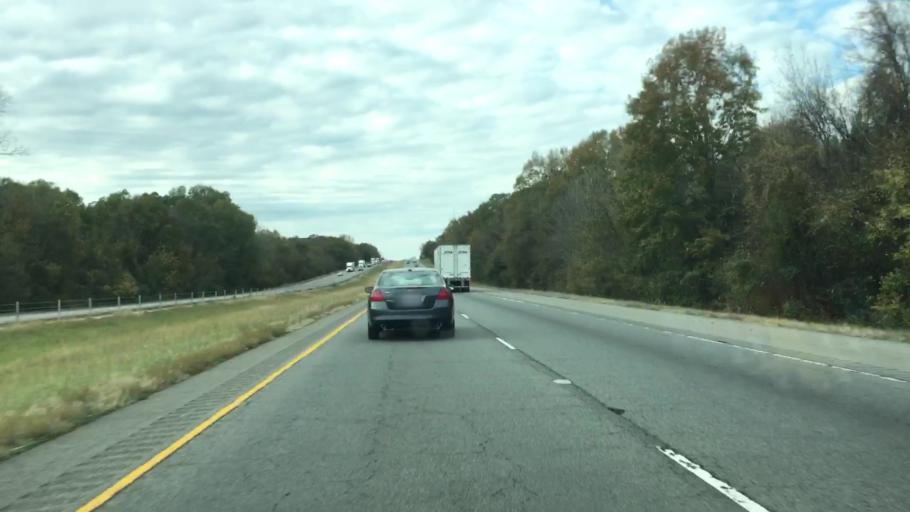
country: US
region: Arkansas
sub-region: Faulkner County
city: Conway
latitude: 35.1405
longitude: -92.5265
